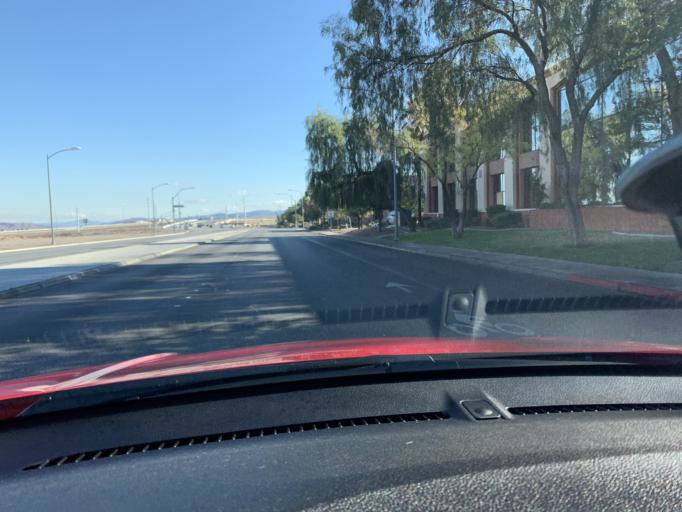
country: US
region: Nevada
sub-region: Clark County
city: Whitney
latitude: 36.0709
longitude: -115.0450
